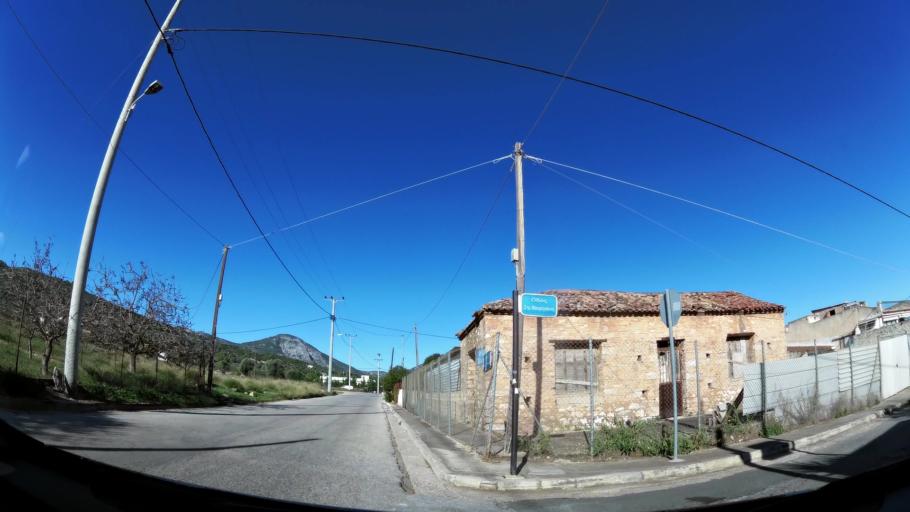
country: GR
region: Attica
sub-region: Nomarchia Anatolikis Attikis
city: Koropi
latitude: 37.8975
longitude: 23.8617
